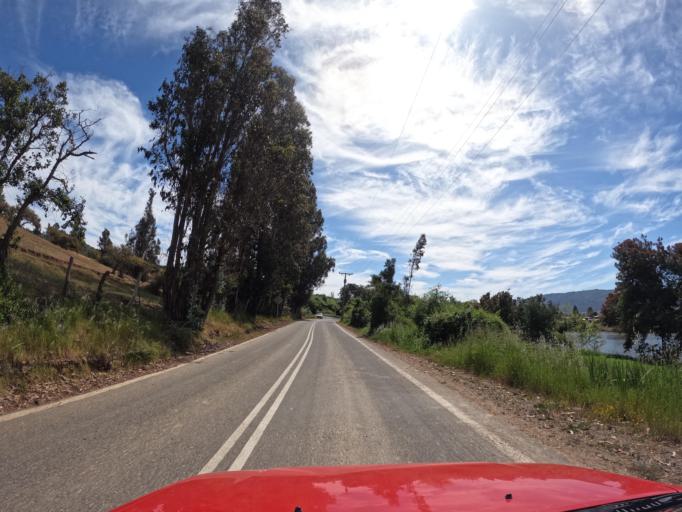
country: CL
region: Maule
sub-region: Provincia de Talca
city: Talca
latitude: -35.0099
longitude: -71.9653
